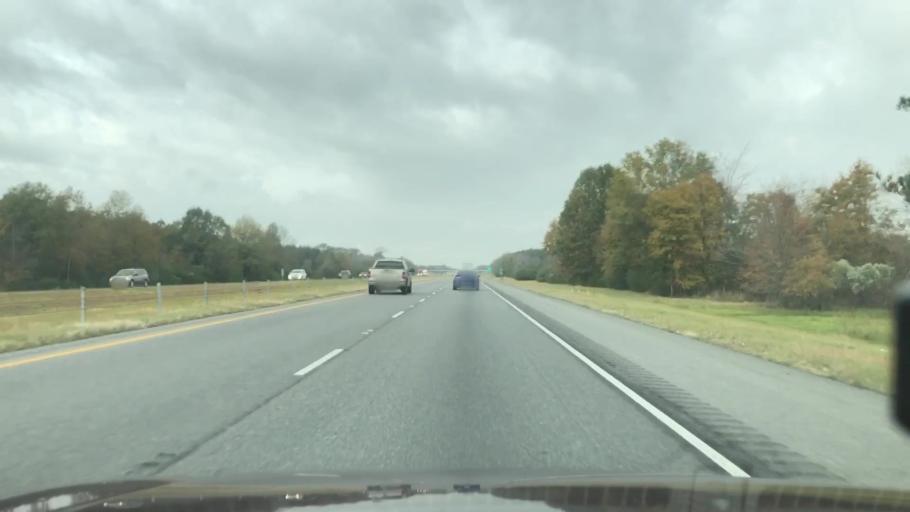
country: US
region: Louisiana
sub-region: Richland Parish
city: Delhi
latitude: 32.4496
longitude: -91.5694
